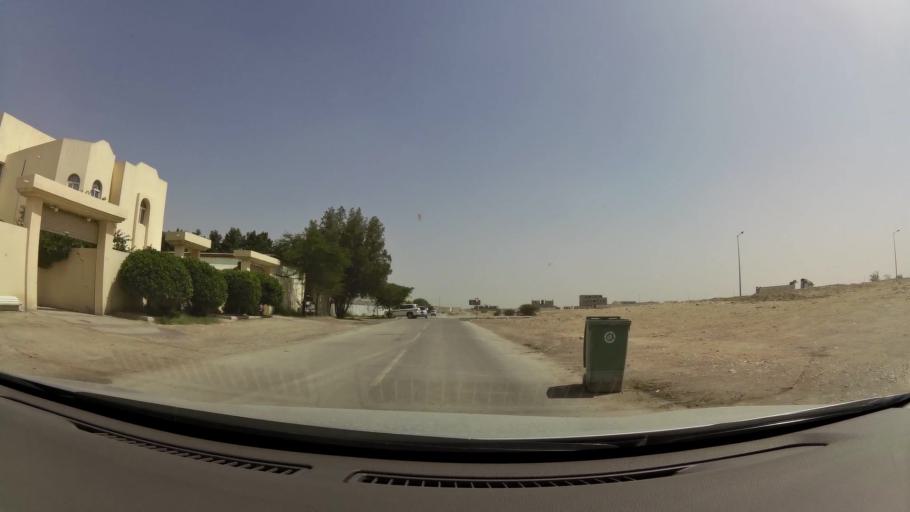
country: QA
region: Baladiyat Umm Salal
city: Umm Salal Muhammad
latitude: 25.3762
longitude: 51.4170
